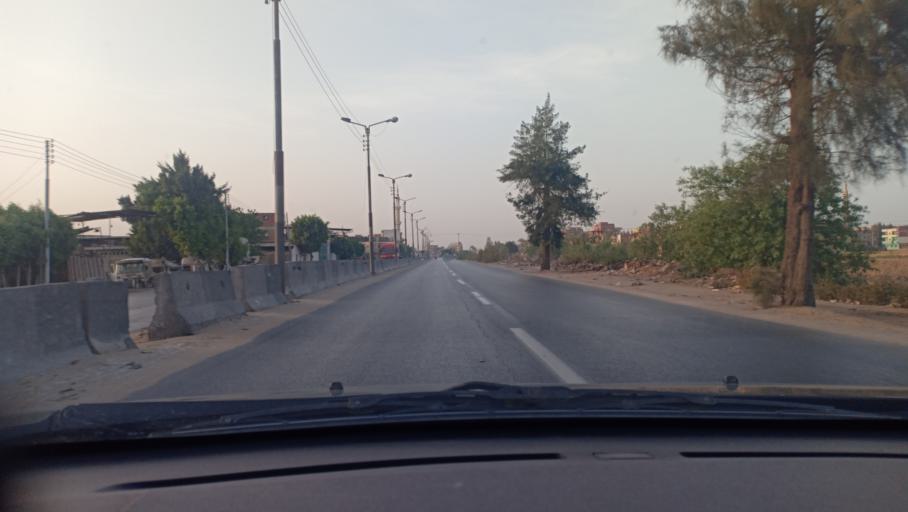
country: EG
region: Muhafazat al Gharbiyah
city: Zifta
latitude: 30.6659
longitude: 31.2853
